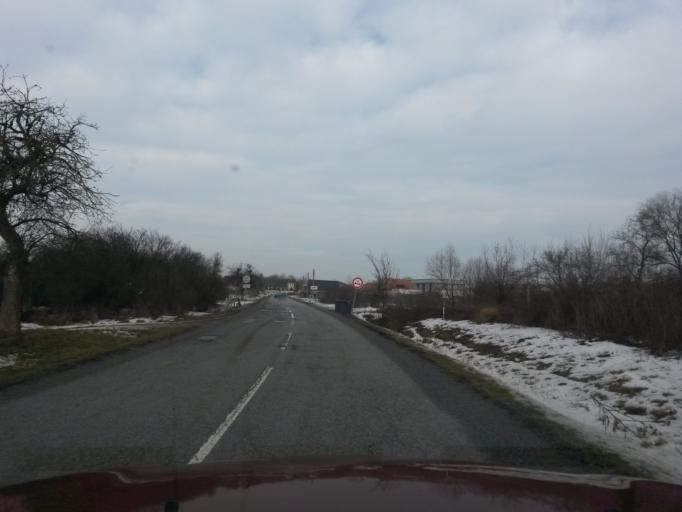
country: SK
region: Kosicky
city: Kosice
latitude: 48.7785
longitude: 21.3311
